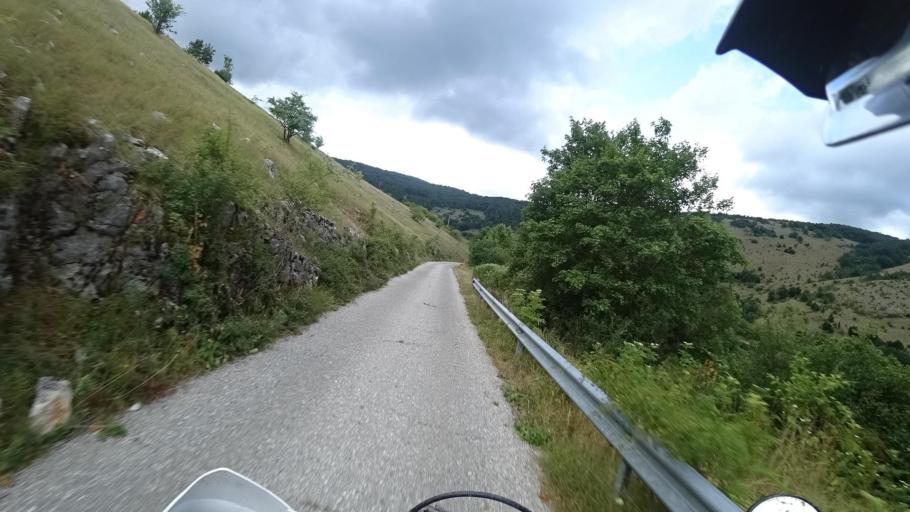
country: HR
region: Licko-Senjska
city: Jezerce
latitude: 44.7391
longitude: 15.4947
